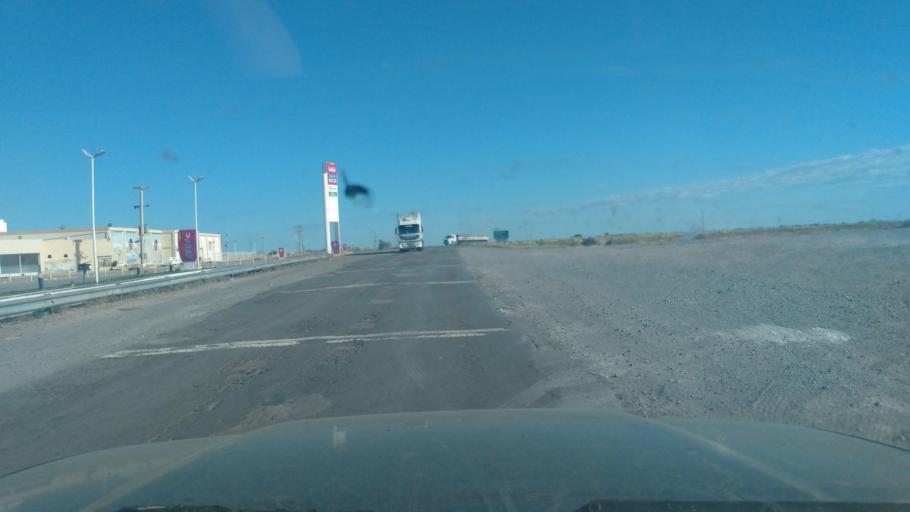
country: AR
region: La Pampa
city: Veinticinco de Mayo
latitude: -37.6619
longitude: -67.7491
